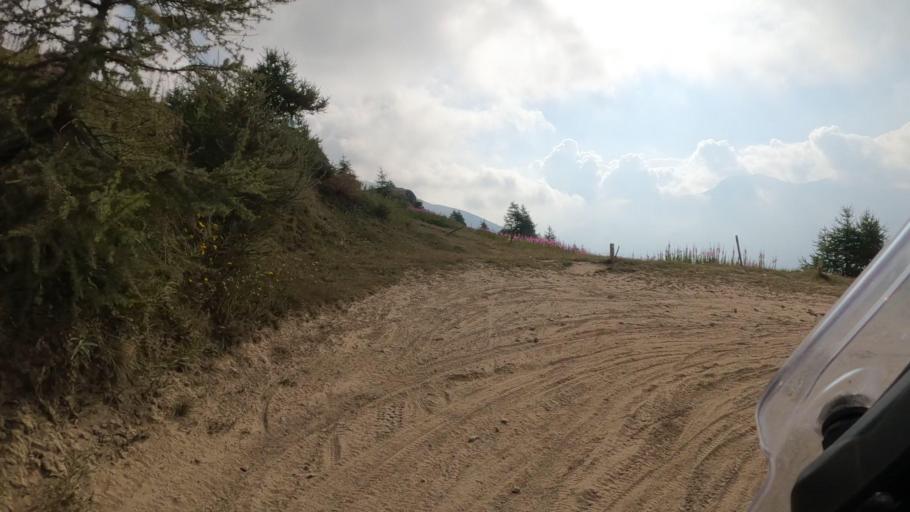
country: IT
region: Piedmont
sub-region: Provincia di Torino
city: Sauze d'Oulx
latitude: 45.0253
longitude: 6.9018
